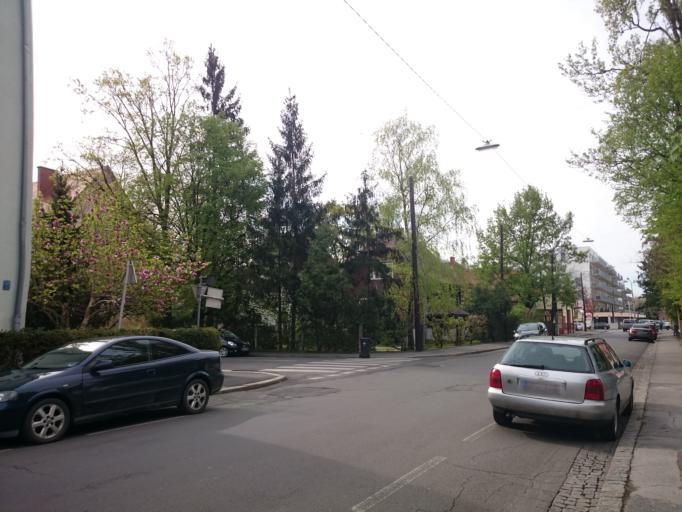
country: AT
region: Styria
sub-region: Graz Stadt
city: Wetzelsdorf
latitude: 47.0715
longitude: 15.4045
